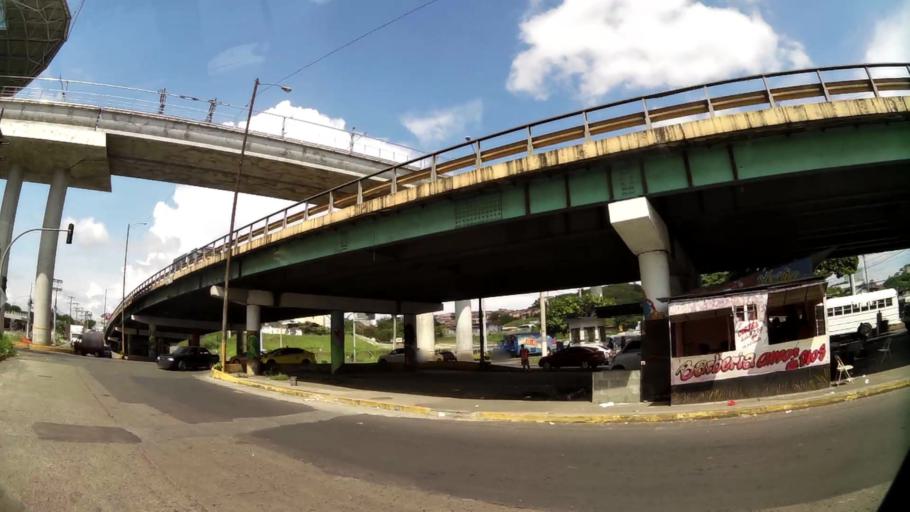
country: PA
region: Panama
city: Panama
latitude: 9.0306
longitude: -79.5060
